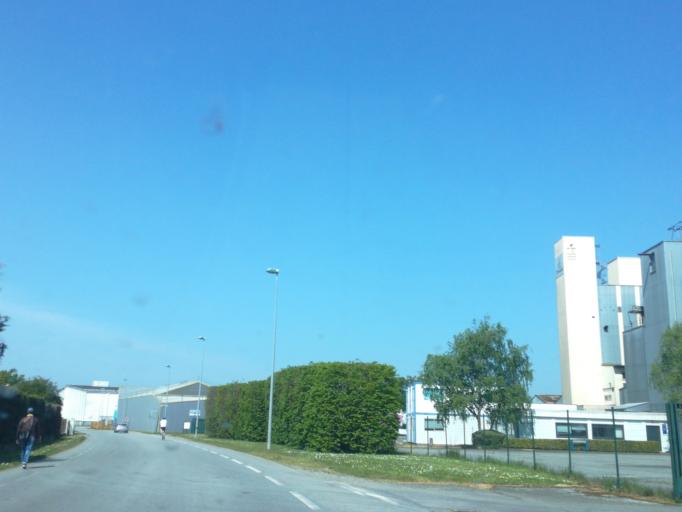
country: FR
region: Brittany
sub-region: Departement du Morbihan
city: Le Sourn
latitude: 48.0473
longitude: -2.9609
